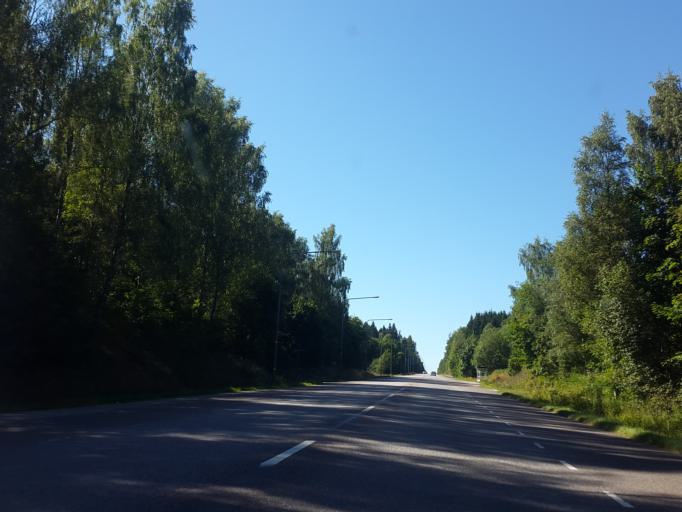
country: SE
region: Vaestra Goetaland
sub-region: Boras Kommun
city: Boras
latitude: 57.7701
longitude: 12.9739
